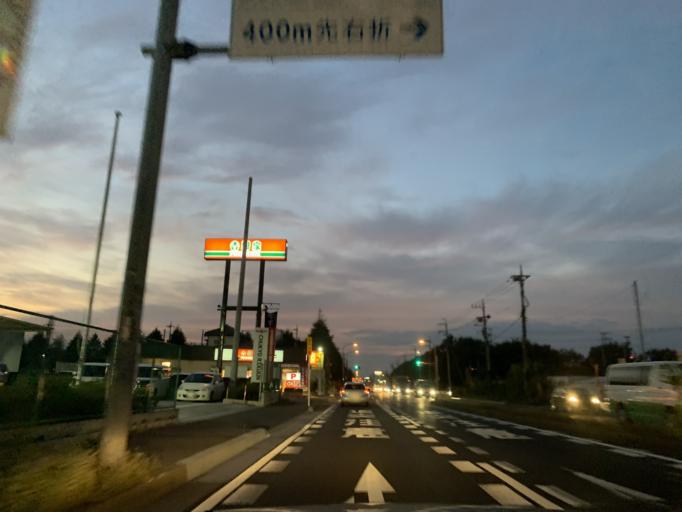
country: JP
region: Chiba
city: Noda
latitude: 35.9242
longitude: 139.9156
